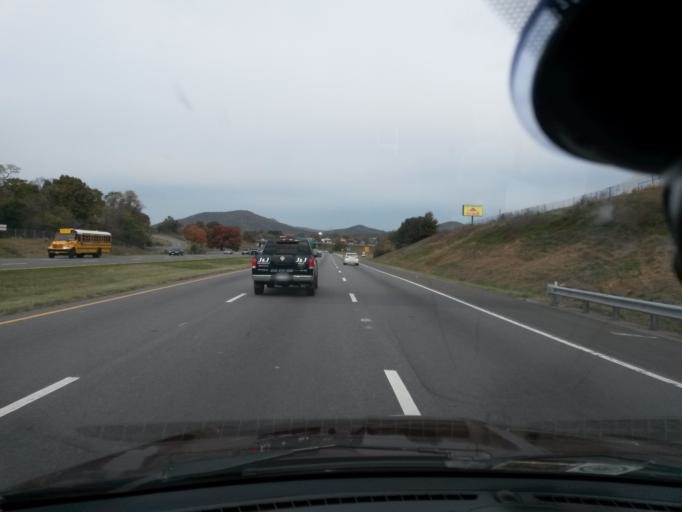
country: US
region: Virginia
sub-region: Roanoke County
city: Hollins
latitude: 37.3227
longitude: -79.9858
